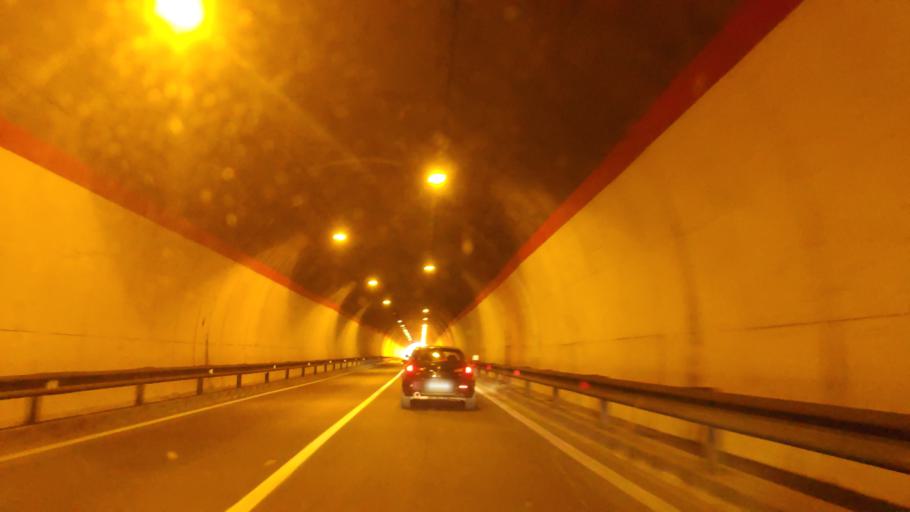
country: IT
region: Calabria
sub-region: Provincia di Cosenza
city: Marina
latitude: 39.4706
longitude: 15.9798
